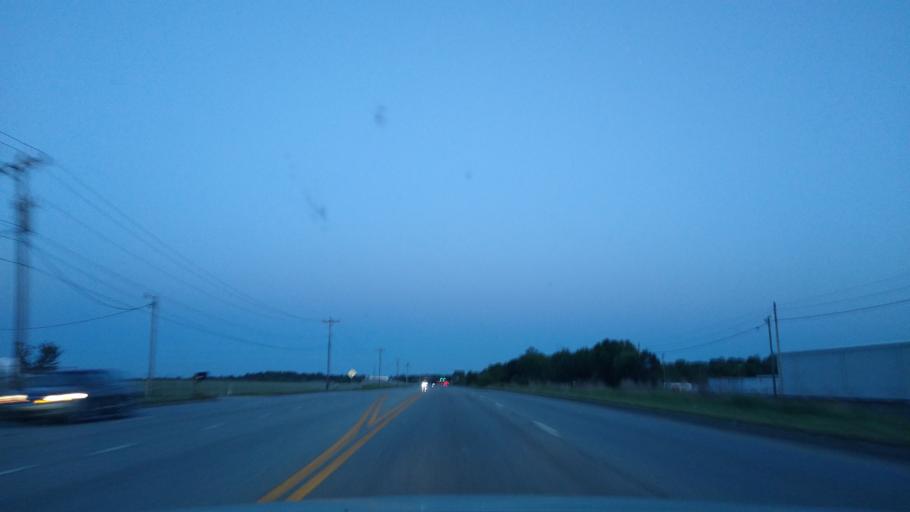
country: US
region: North Carolina
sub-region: Guilford County
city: Jamestown
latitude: 36.0871
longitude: -79.9422
